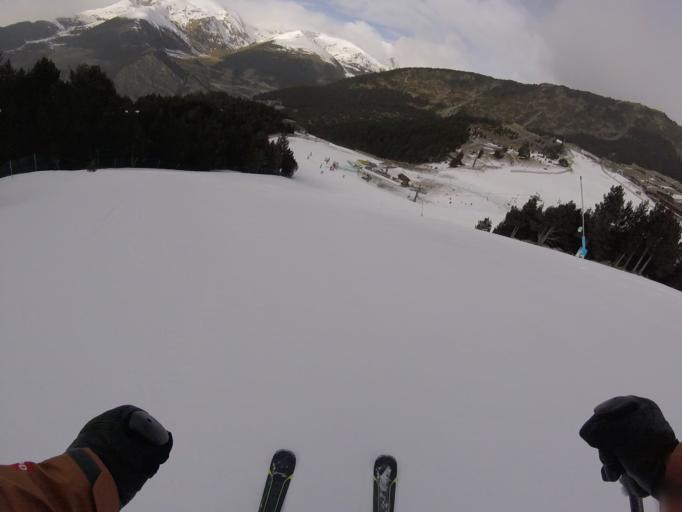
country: AD
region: Canillo
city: Canillo
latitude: 42.5526
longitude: 1.6133
